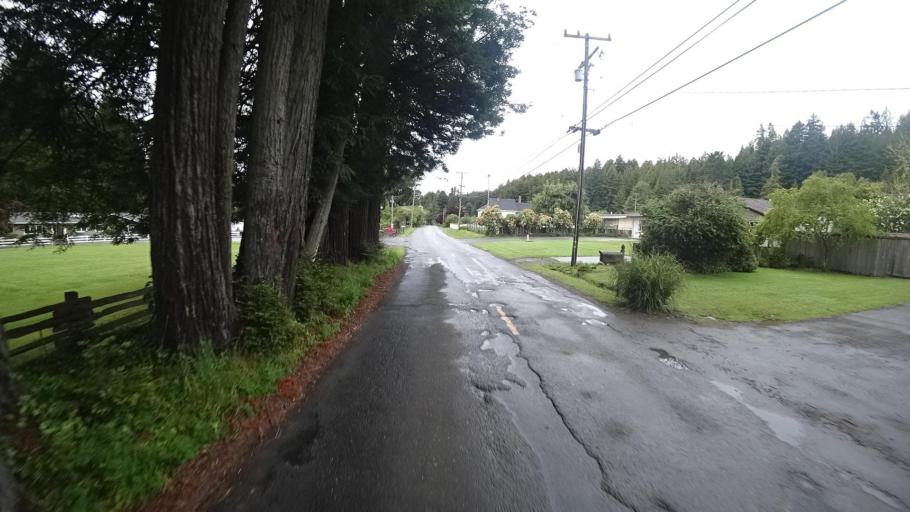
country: US
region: California
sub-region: Humboldt County
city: Bayside
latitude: 40.8309
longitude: -124.0406
